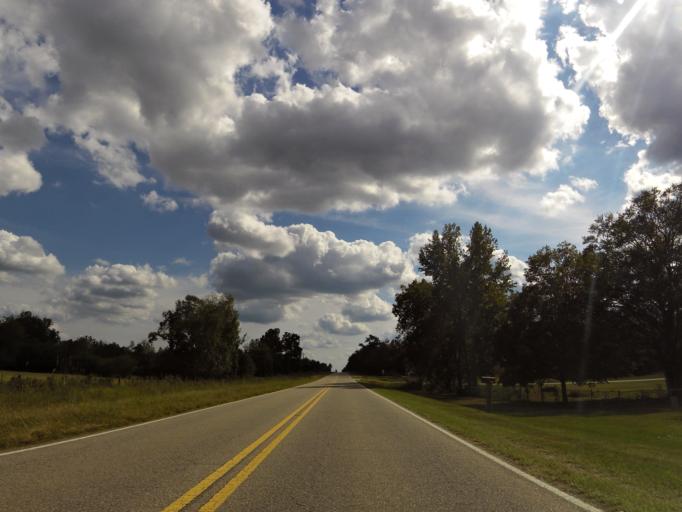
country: US
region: Alabama
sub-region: Dallas County
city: Selmont-West Selmont
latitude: 32.2659
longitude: -86.9903
